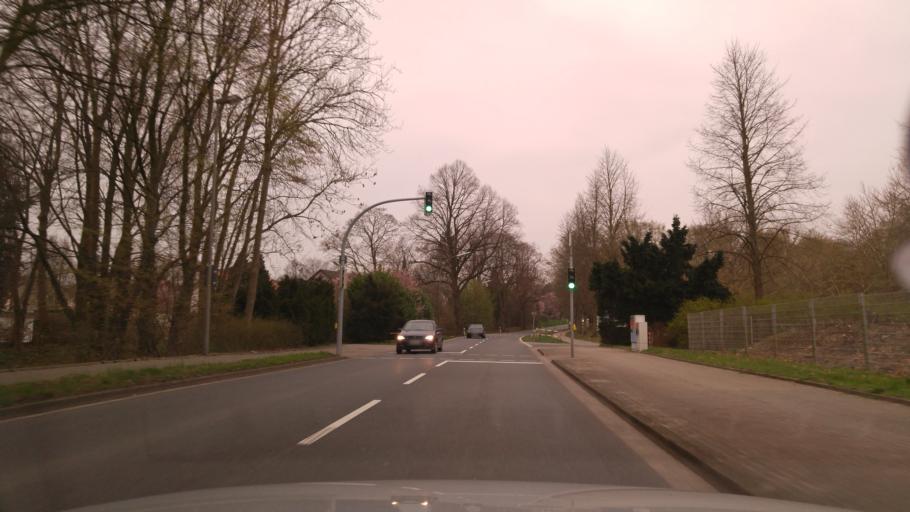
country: DE
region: North Rhine-Westphalia
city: Lanstrop
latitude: 51.5152
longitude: 7.5524
